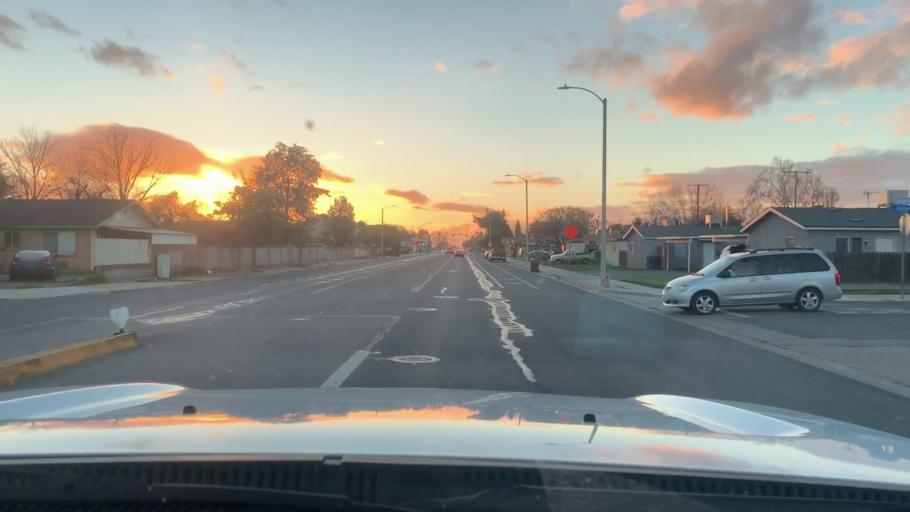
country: US
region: California
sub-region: Tulare County
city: Tulare
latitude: 36.1965
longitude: -119.3492
